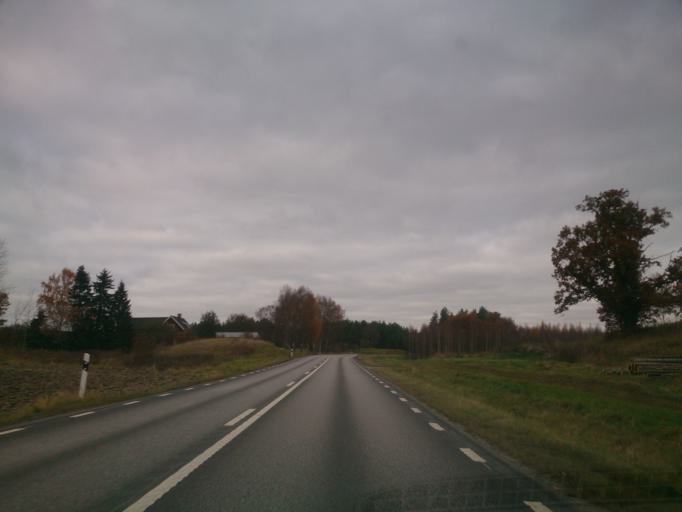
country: SE
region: OEstergoetland
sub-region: Linkopings Kommun
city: Sturefors
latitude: 58.3220
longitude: 15.8640
